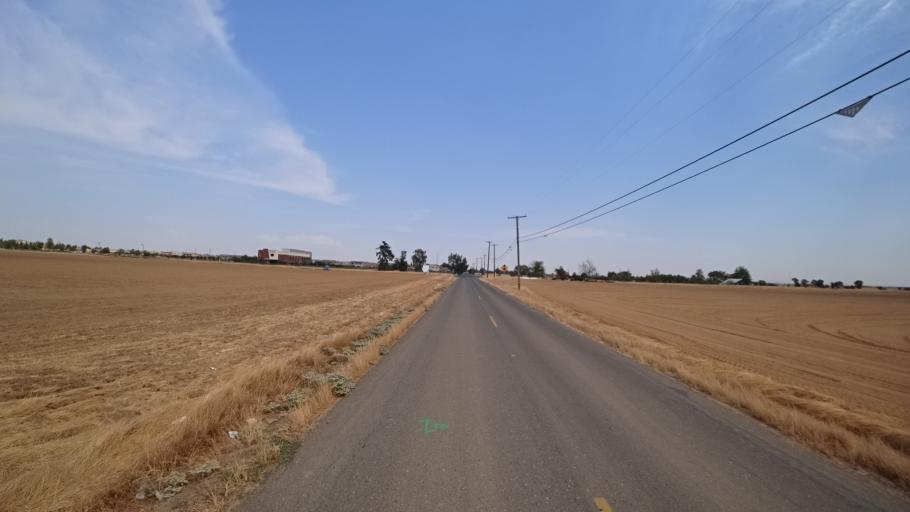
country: US
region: California
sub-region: Sacramento County
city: Elk Grove
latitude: 38.3908
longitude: -121.4012
